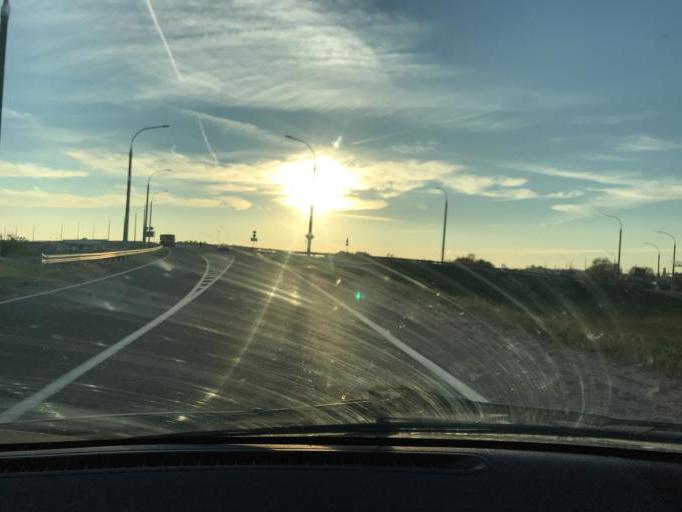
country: BY
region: Brest
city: Horad Kobryn
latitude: 52.2166
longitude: 24.4027
